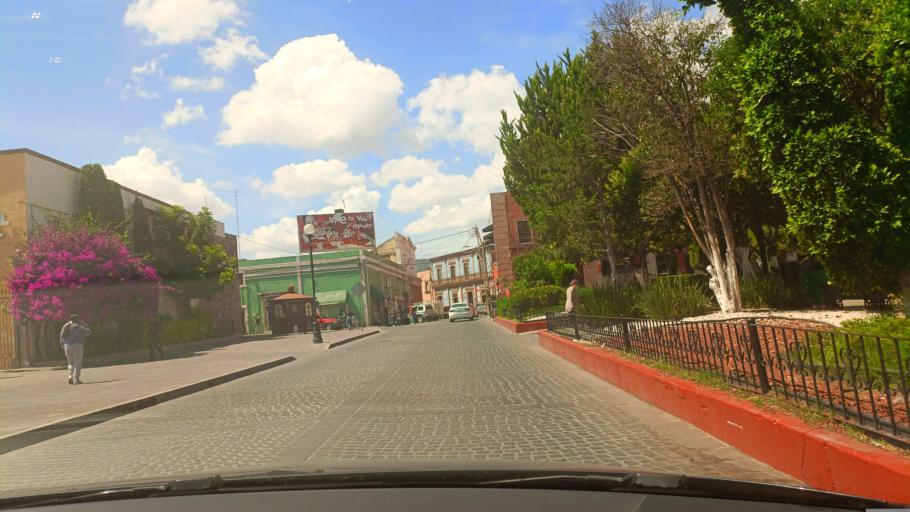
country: MX
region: Guanajuato
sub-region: San Luis de la Paz
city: San Luis de la Paz
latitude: 21.2987
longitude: -100.5145
